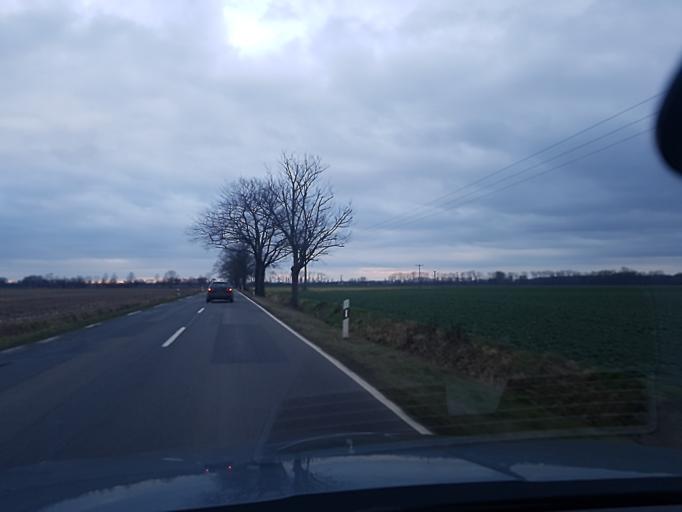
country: DE
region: Brandenburg
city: Schonewalde
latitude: 51.6884
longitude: 13.6172
